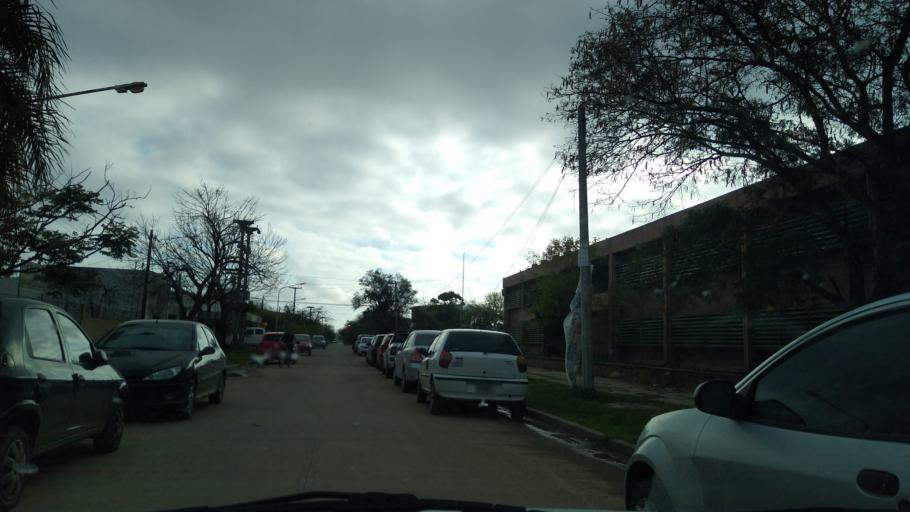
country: AR
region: Chaco
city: Barranqueras
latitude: -27.4882
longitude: -58.9367
